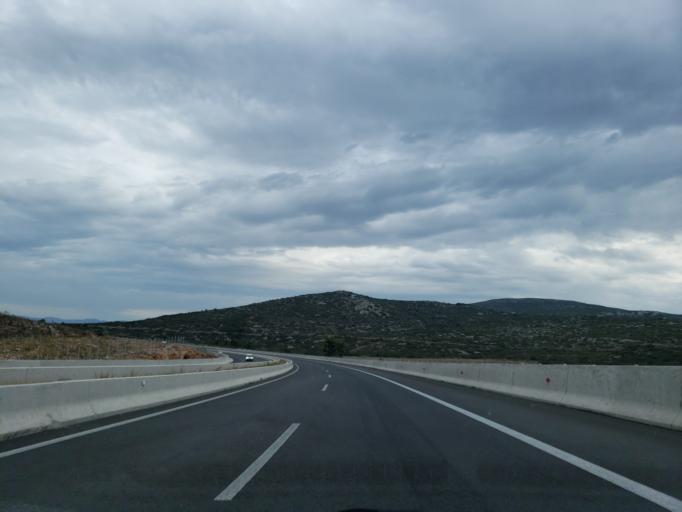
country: GR
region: Central Greece
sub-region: Nomos Voiotias
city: Akraifnia
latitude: 38.3826
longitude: 23.2466
